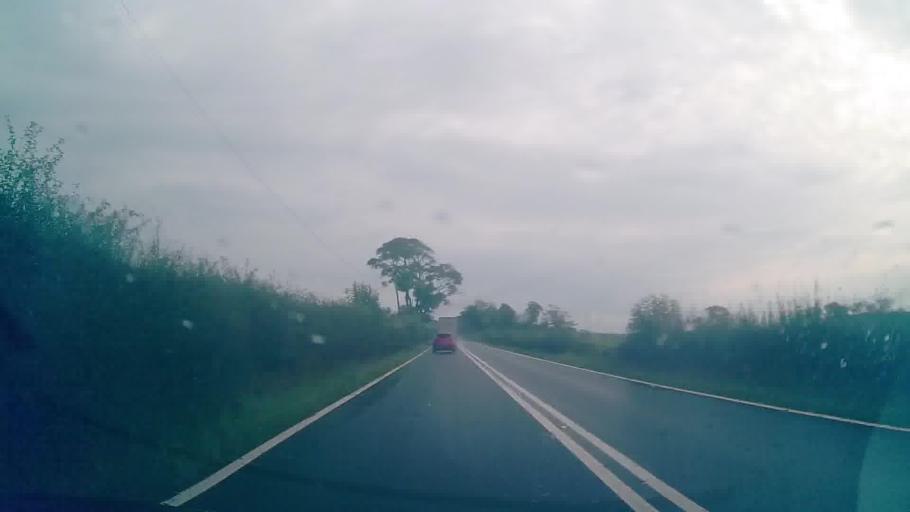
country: GB
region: Scotland
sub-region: Dumfries and Galloway
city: Lochmaben
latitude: 55.0621
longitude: -3.4904
